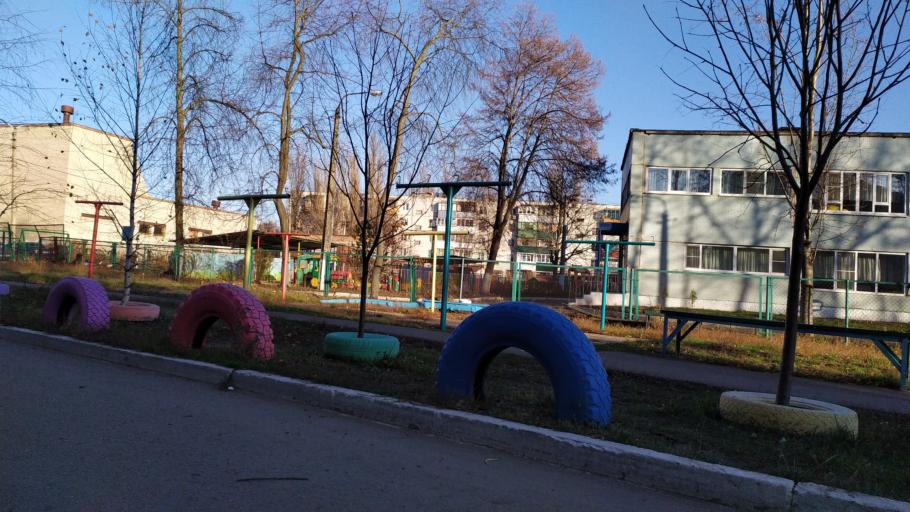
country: RU
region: Kursk
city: Kursk
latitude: 51.6483
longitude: 36.1375
